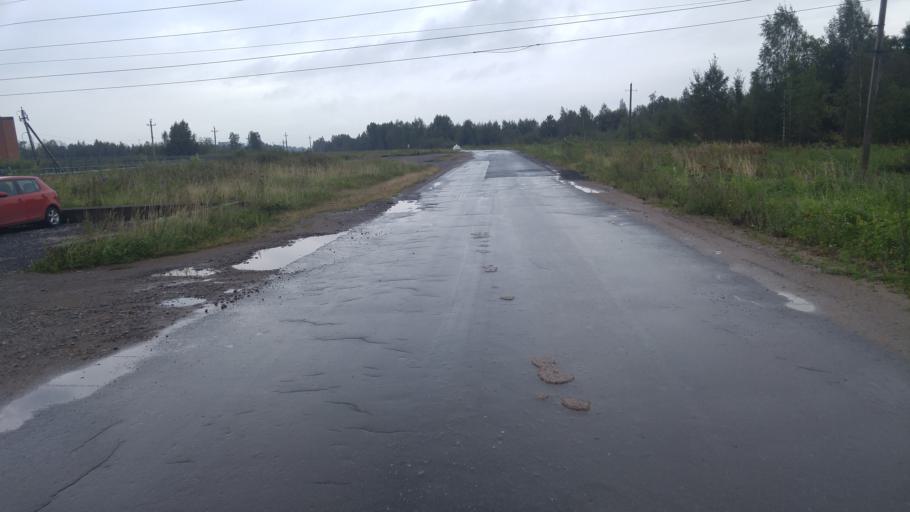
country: RU
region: St.-Petersburg
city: Metallostroy
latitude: 59.7804
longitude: 30.5683
